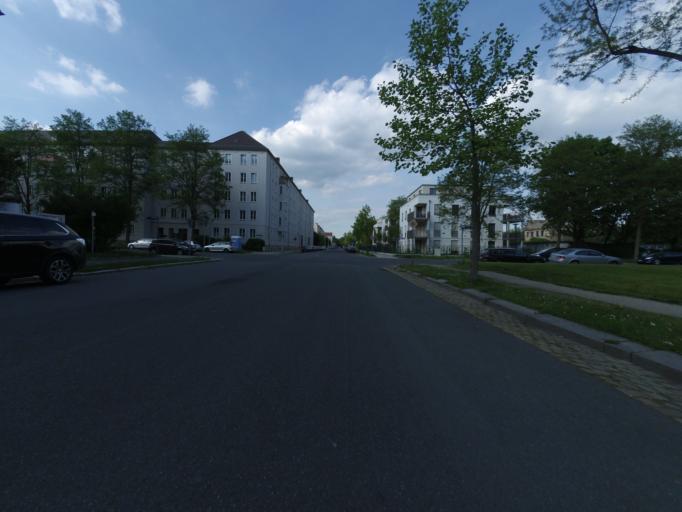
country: DE
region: Saxony
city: Dresden
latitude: 51.0414
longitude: 13.7775
